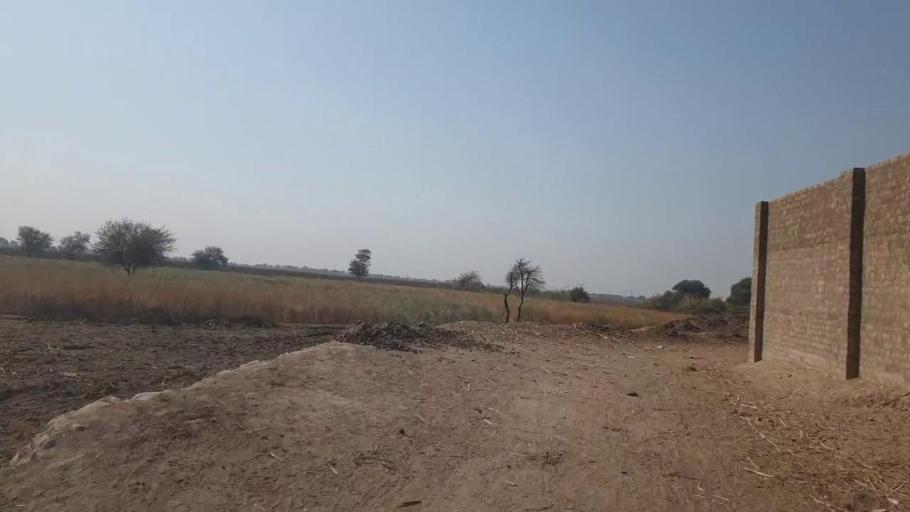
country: PK
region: Sindh
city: Tando Adam
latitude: 25.6269
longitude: 68.7173
